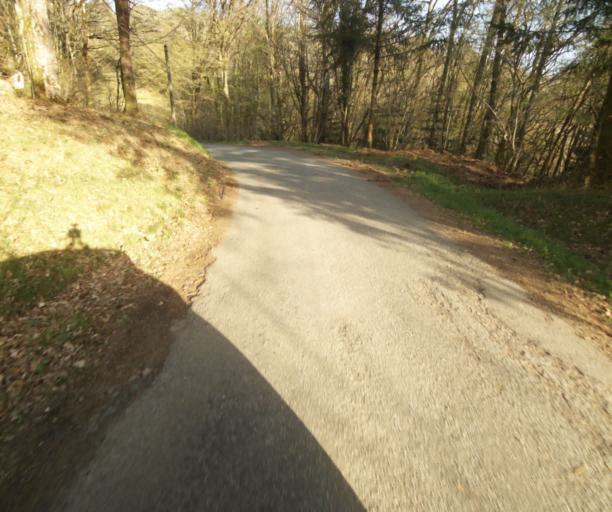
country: FR
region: Limousin
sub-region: Departement de la Correze
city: Correze
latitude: 45.3840
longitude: 1.8396
